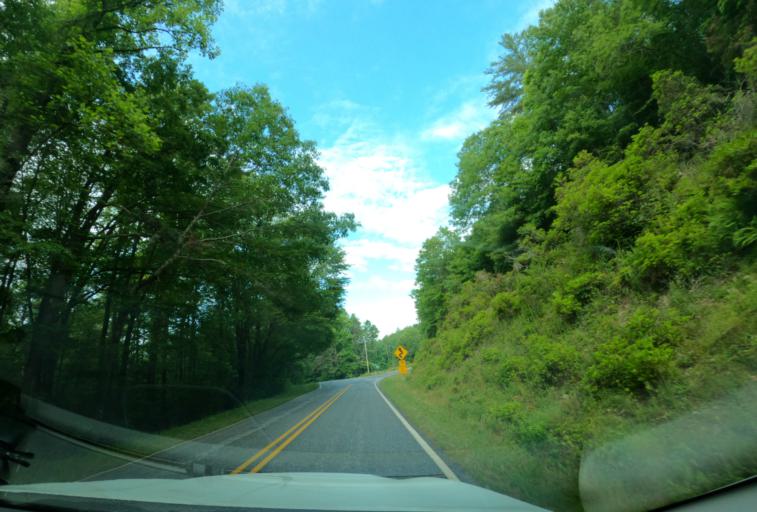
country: US
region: North Carolina
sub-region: Transylvania County
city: Brevard
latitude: 35.1913
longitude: -82.9013
